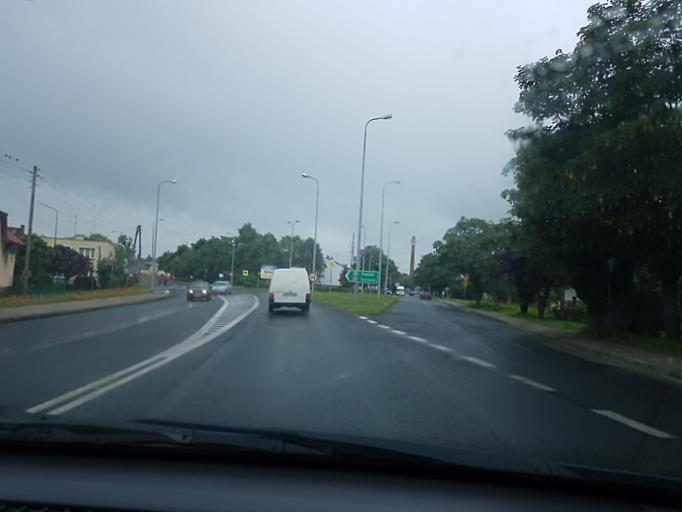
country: PL
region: Lodz Voivodeship
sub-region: Powiat kutnowski
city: Kutno
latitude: 52.2324
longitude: 19.3487
